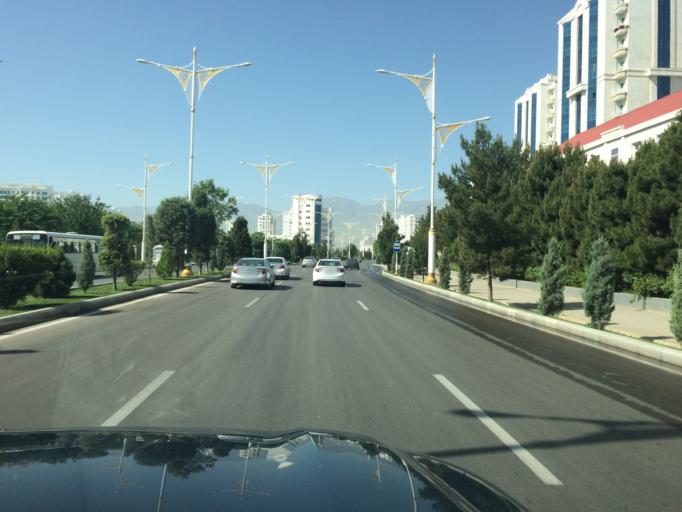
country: TM
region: Ahal
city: Ashgabat
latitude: 37.9145
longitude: 58.3705
